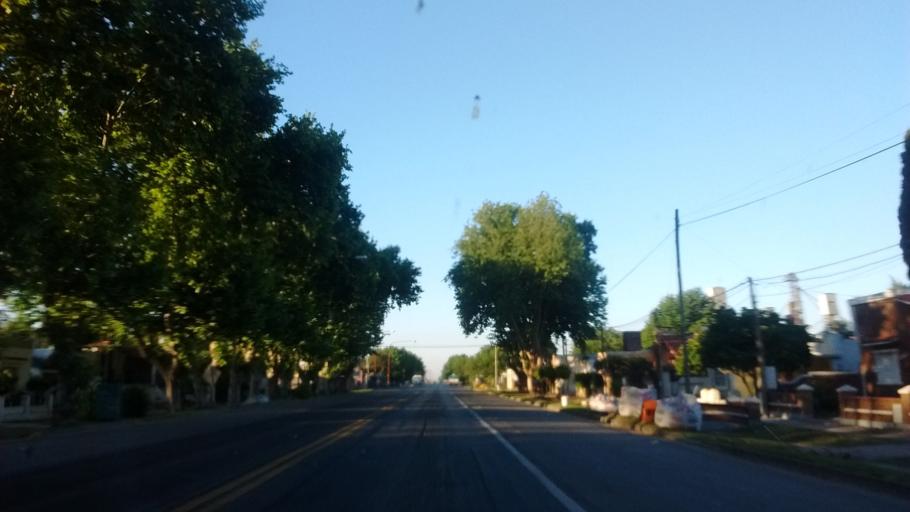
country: AR
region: Santa Fe
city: Firmat
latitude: -33.2479
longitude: -61.3614
